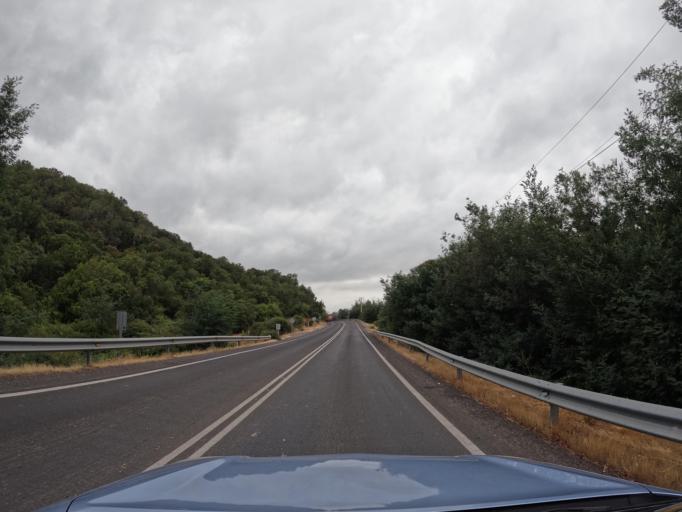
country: CL
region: O'Higgins
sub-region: Provincia de Colchagua
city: Chimbarongo
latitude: -34.7265
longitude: -71.0943
